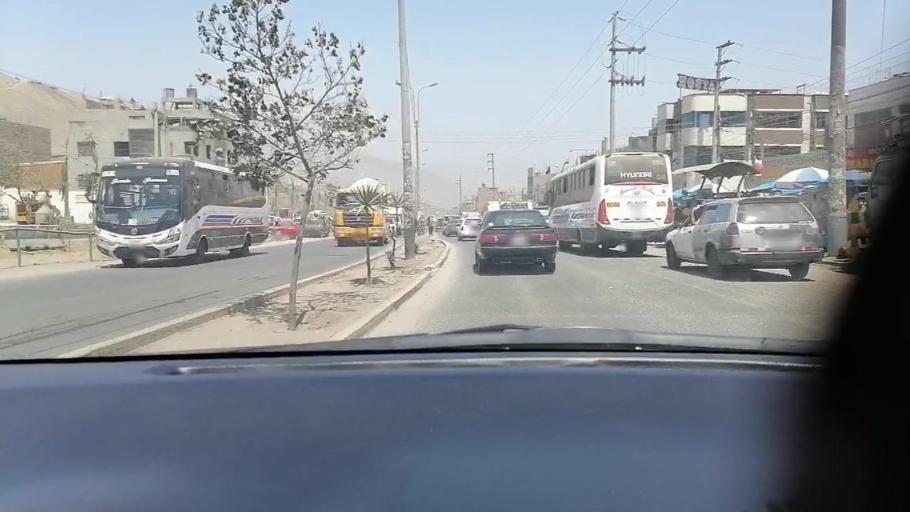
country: PE
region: Lima
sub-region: Lima
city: La Molina
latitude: -12.0841
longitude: -76.8778
